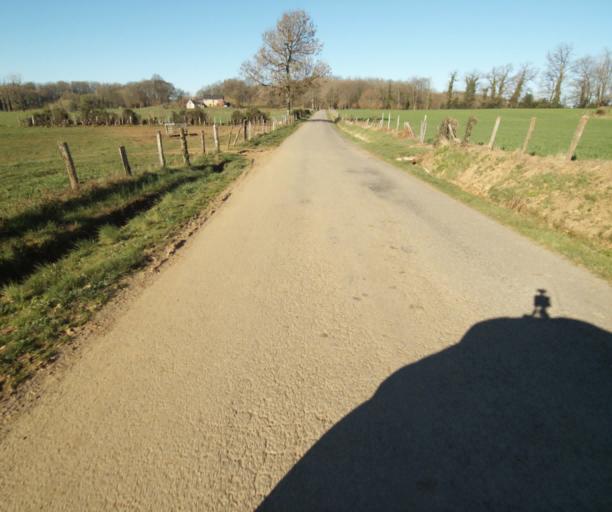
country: FR
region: Limousin
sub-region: Departement de la Correze
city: Saint-Clement
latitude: 45.3883
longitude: 1.6358
